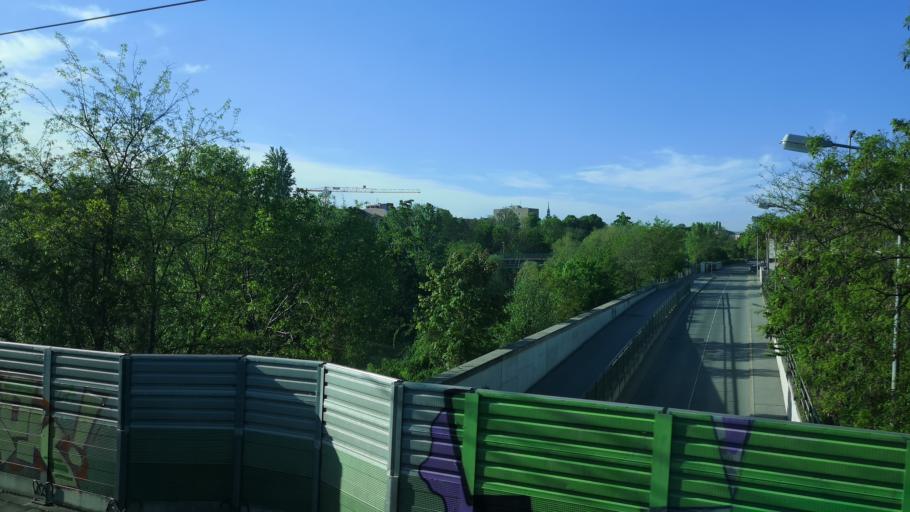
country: AT
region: Lower Austria
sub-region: Politischer Bezirk Wien-Umgebung
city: Schwechat
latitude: 48.1460
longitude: 16.4761
